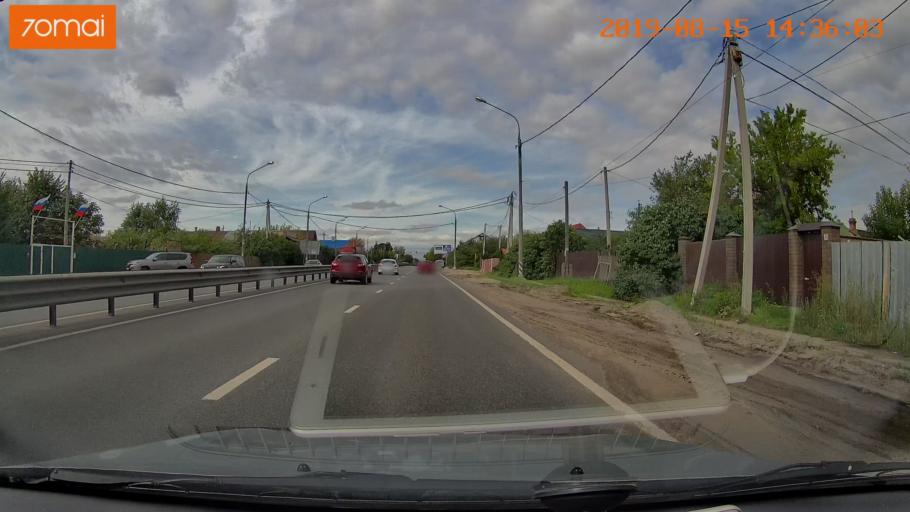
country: RU
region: Moskovskaya
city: Tomilino
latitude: 55.6432
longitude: 37.9362
